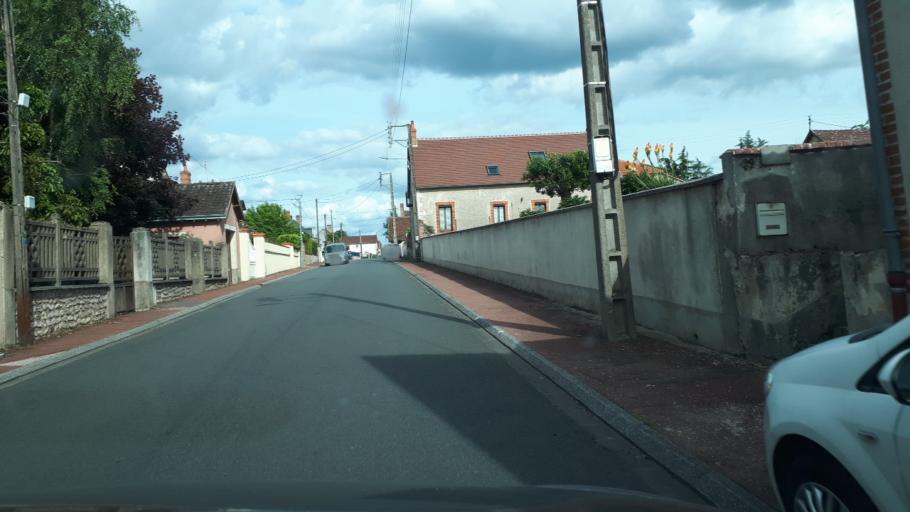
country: FR
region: Centre
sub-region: Departement du Loir-et-Cher
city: Romorantin-Lanthenay
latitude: 47.3530
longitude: 1.7519
